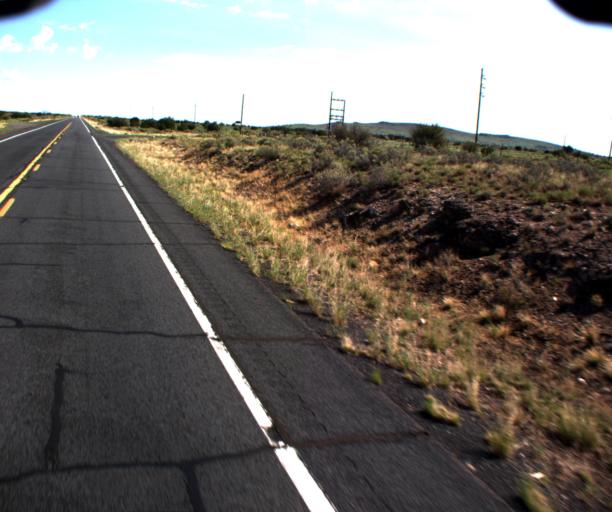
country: US
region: Arizona
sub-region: Coconino County
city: Williams
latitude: 35.5258
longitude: -112.1677
